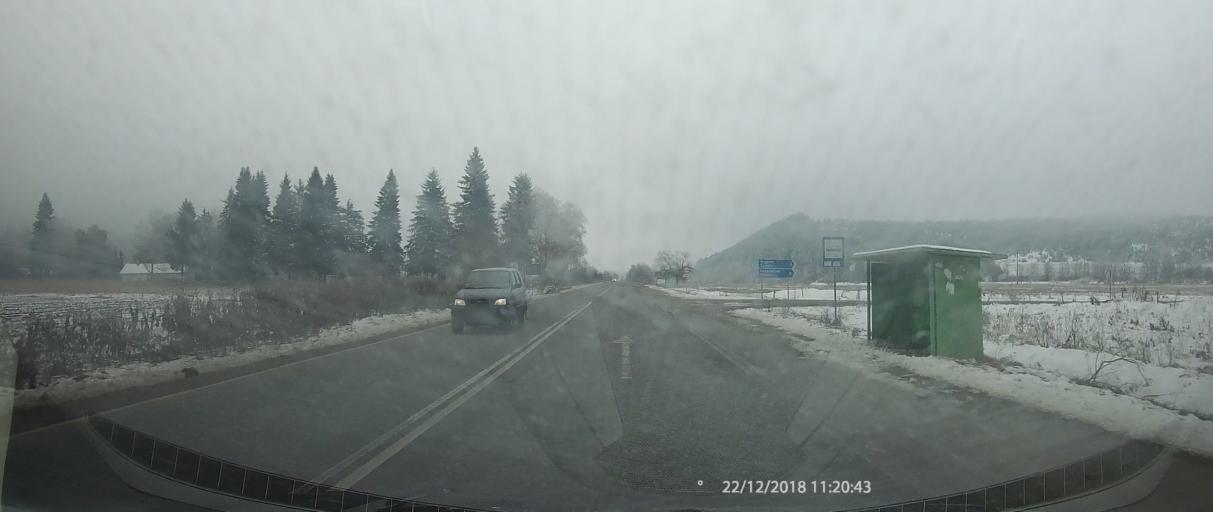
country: BG
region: Kyustendil
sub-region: Obshtina Kyustendil
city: Kyustendil
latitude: 42.2626
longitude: 22.8243
